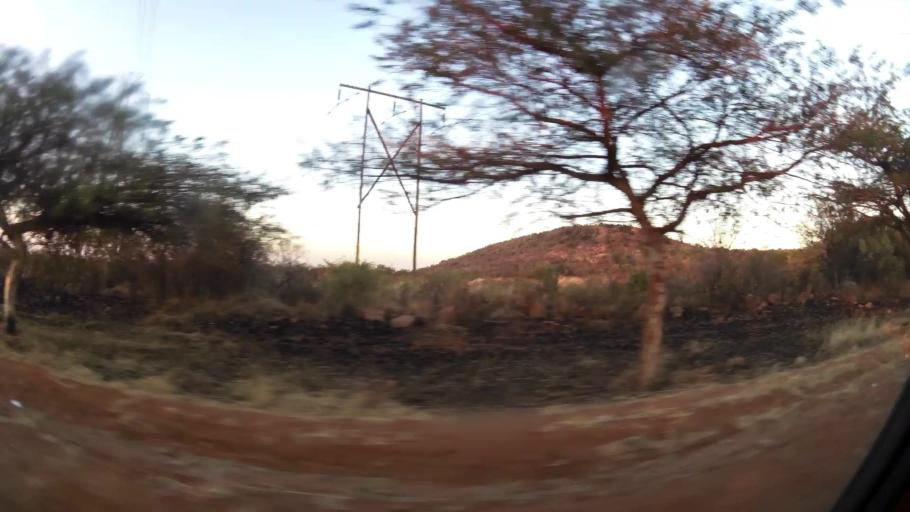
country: ZA
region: North-West
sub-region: Bojanala Platinum District Municipality
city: Rustenburg
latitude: -25.6124
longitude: 27.1777
